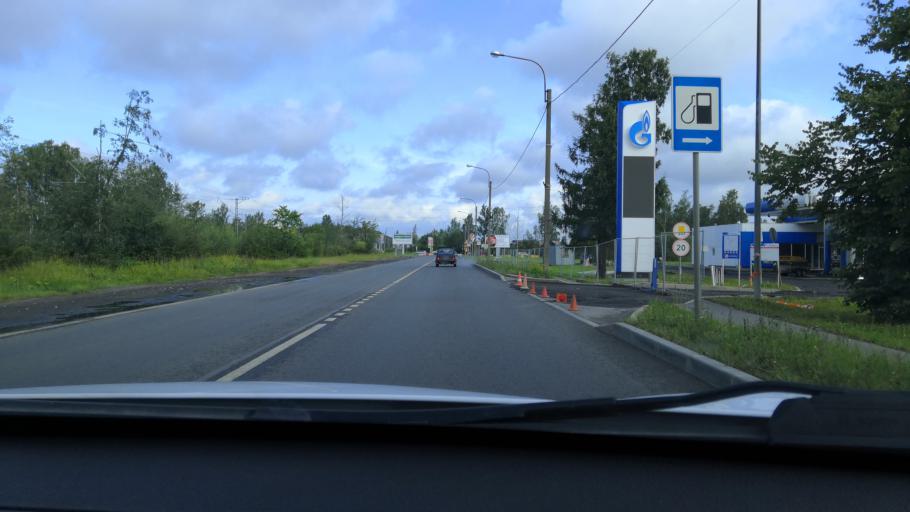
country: RU
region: St.-Petersburg
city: Tyarlevo
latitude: 59.7105
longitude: 30.4364
